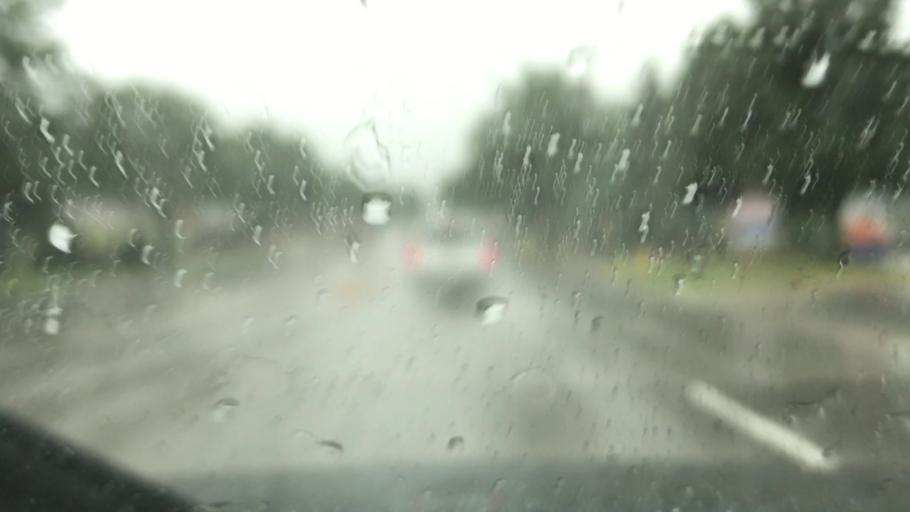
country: US
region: Michigan
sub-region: Kent County
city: Wyoming
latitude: 42.8834
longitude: -85.7241
